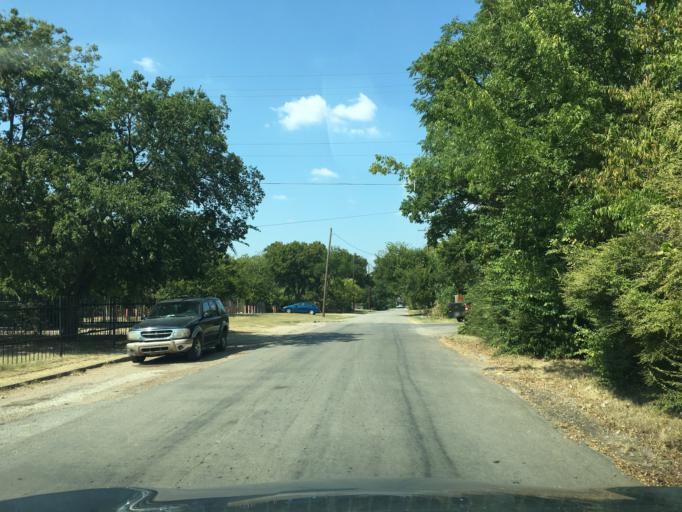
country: US
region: Texas
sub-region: Dallas County
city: Dallas
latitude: 32.7362
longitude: -96.7957
